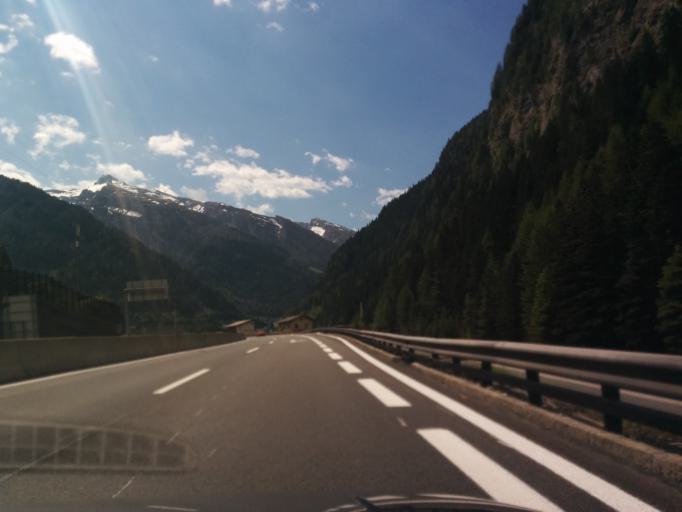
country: AT
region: Tyrol
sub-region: Politischer Bezirk Innsbruck Land
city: Gries am Brenner
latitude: 47.0225
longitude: 11.5018
